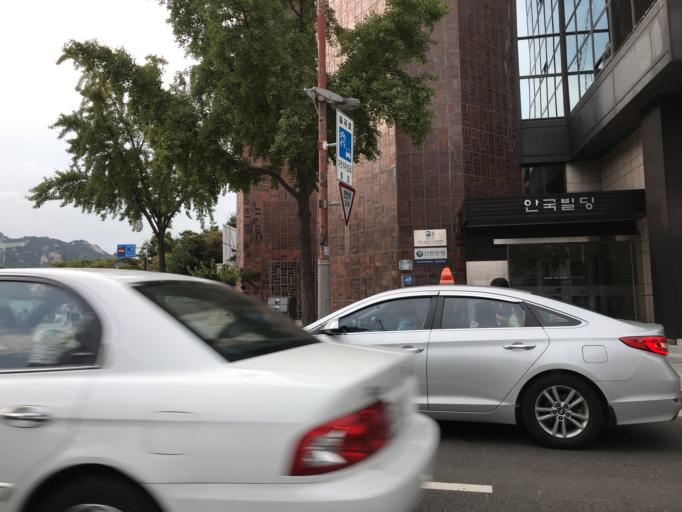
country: KR
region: Seoul
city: Seoul
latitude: 37.5758
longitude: 126.9836
